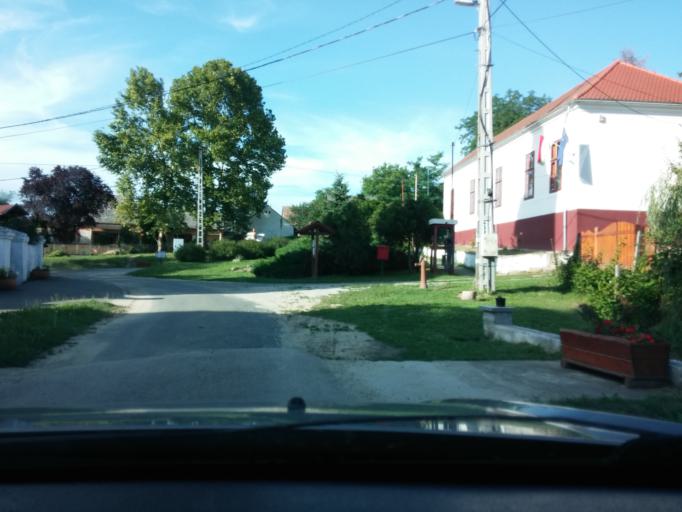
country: HU
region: Somogy
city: Kaposmero
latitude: 46.2713
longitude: 17.7331
